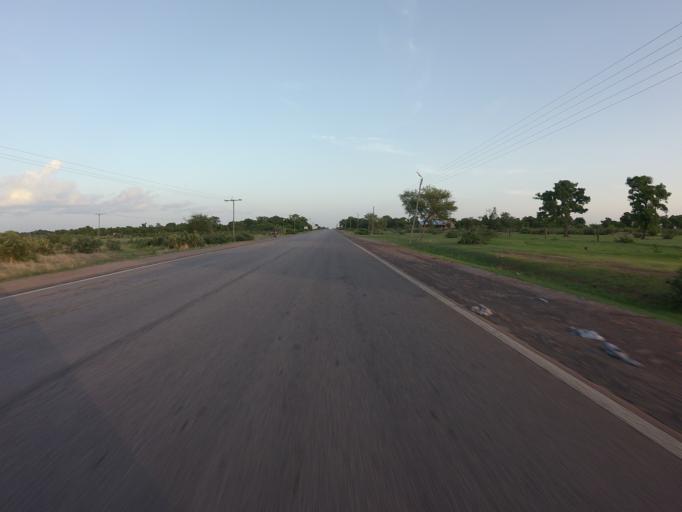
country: GH
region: Upper East
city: Navrongo
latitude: 10.9490
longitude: -1.0948
